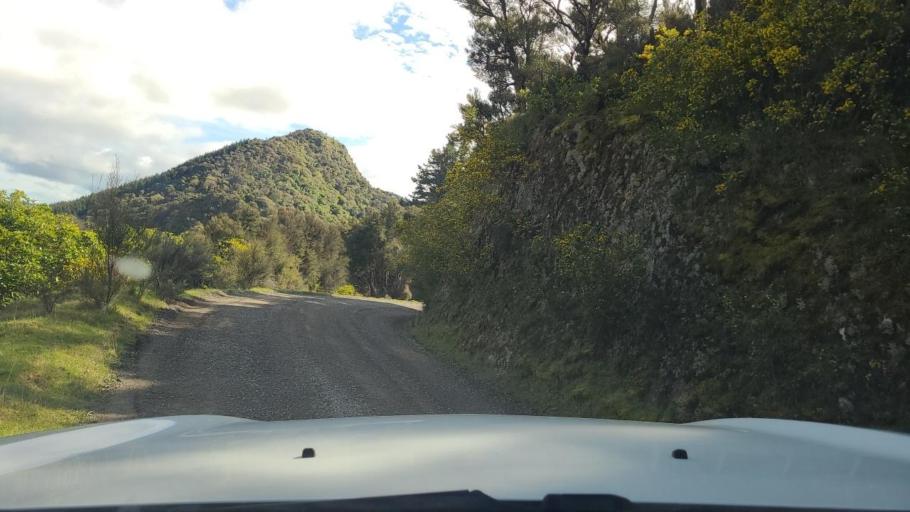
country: NZ
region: Wellington
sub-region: South Wairarapa District
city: Waipawa
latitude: -41.3482
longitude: 175.6791
